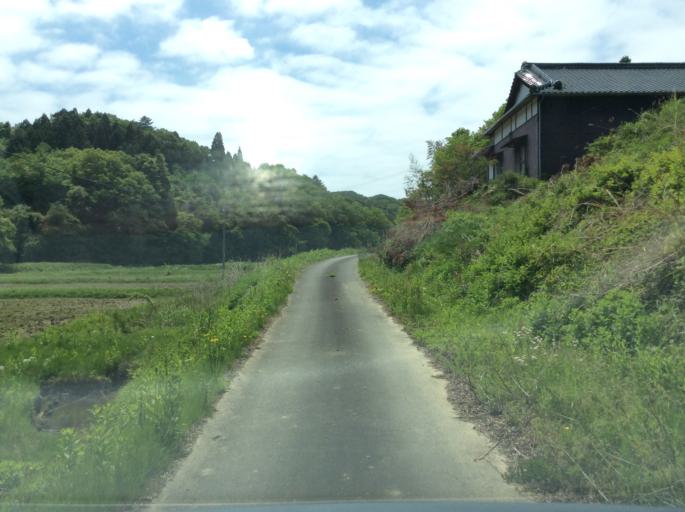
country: JP
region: Fukushima
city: Iwaki
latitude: 37.0079
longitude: 140.9458
